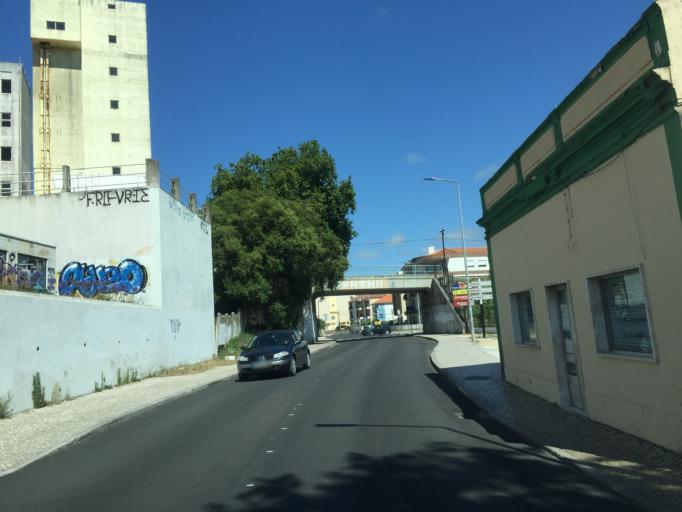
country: PT
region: Leiria
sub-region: Caldas da Rainha
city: Caldas da Rainha
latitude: 39.4022
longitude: -9.1397
